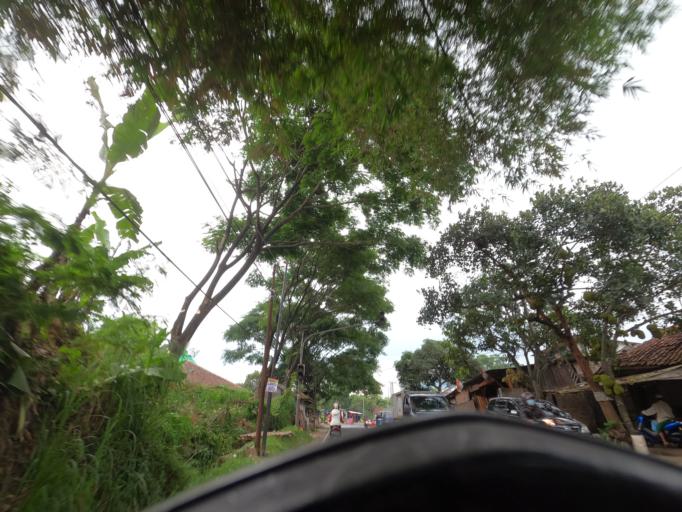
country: ID
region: West Java
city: Sukabumi
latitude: -6.7804
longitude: 107.0629
